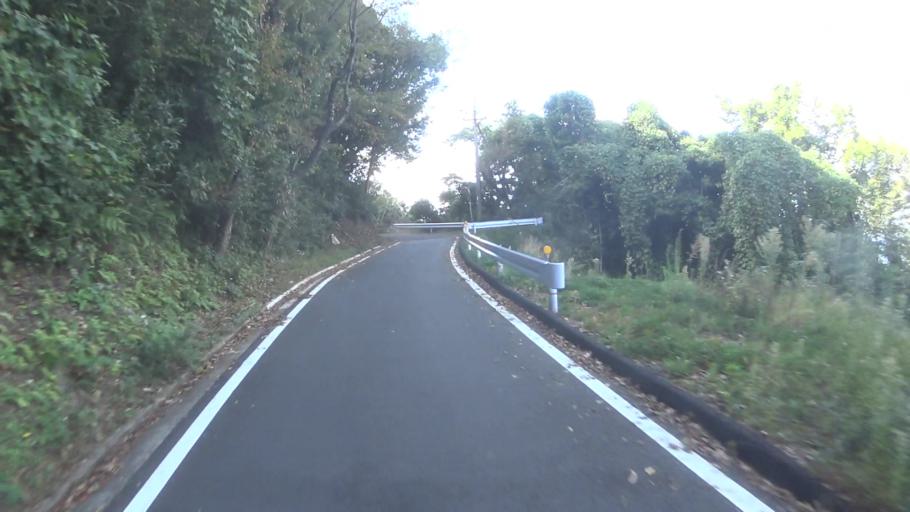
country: JP
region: Kyoto
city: Maizuru
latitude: 35.5680
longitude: 135.4147
